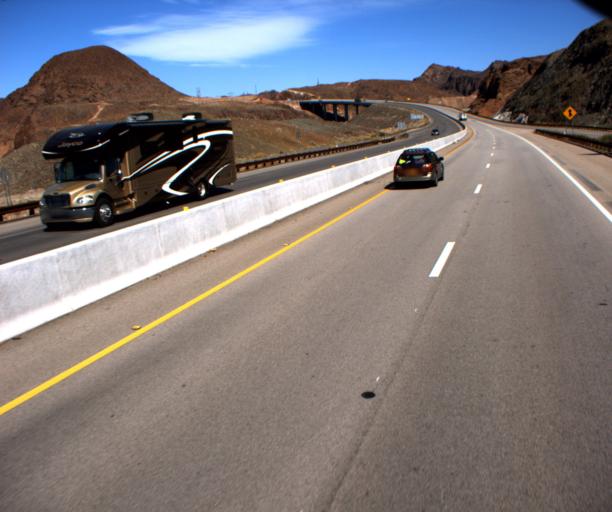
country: US
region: Nevada
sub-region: Clark County
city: Boulder City
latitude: 36.0036
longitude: -114.7233
